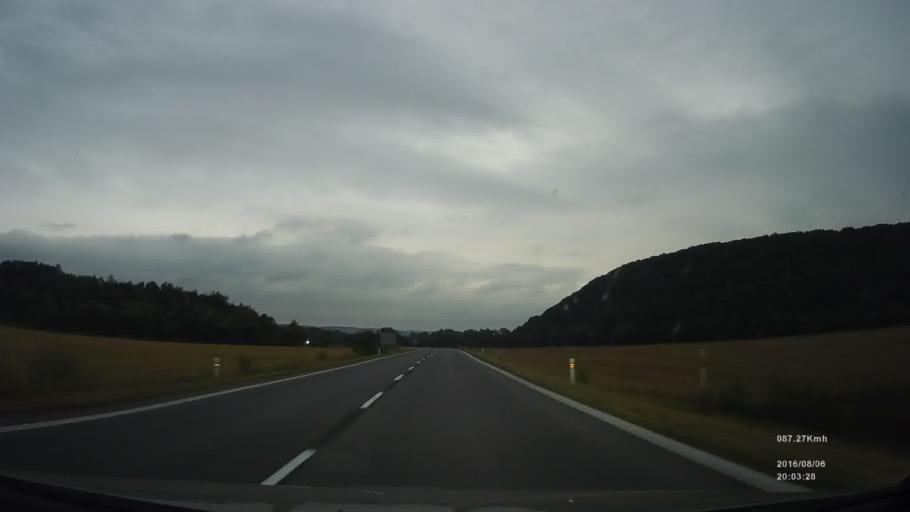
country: SK
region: Presovsky
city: Stropkov
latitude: 49.2489
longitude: 21.6096
